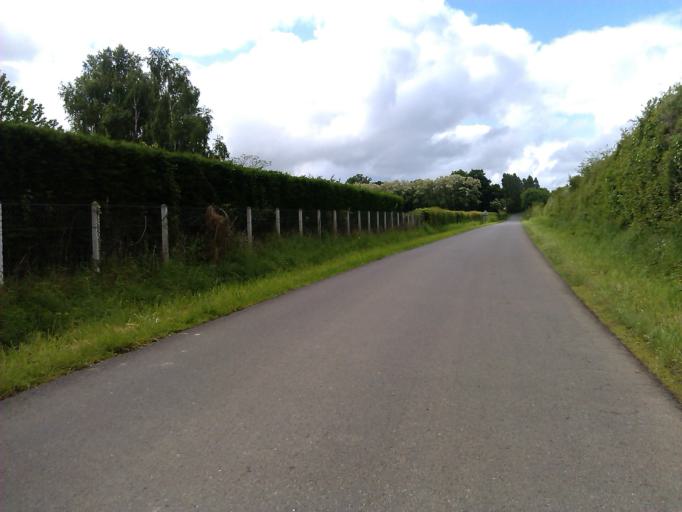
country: FR
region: Poitou-Charentes
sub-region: Departement de la Vienne
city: Availles-Limouzine
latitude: 46.1408
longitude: 0.5932
